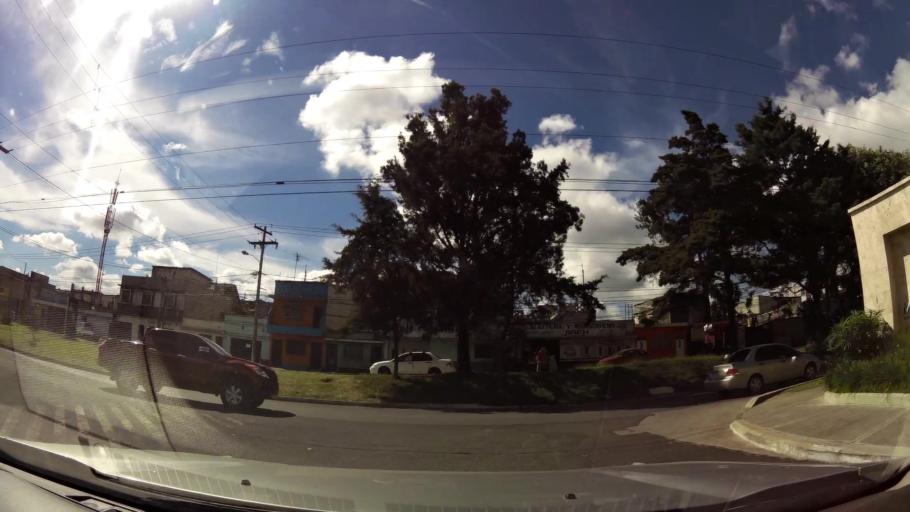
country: GT
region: Guatemala
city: Mixco
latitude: 14.6529
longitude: -90.5690
